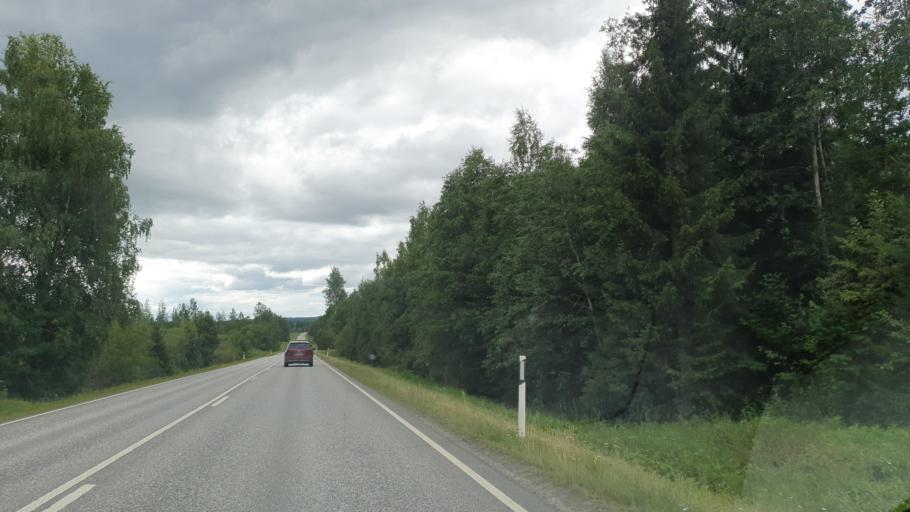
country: FI
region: Northern Savo
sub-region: Ylae-Savo
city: Sonkajaervi
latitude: 63.7385
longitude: 27.3799
